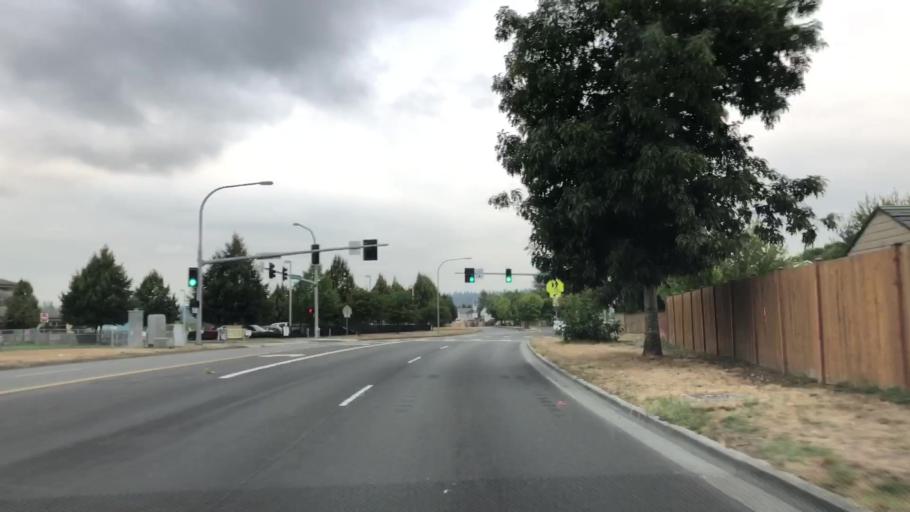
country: US
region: Washington
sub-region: Snohomish County
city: Monroe
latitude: 47.8580
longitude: -122.0114
